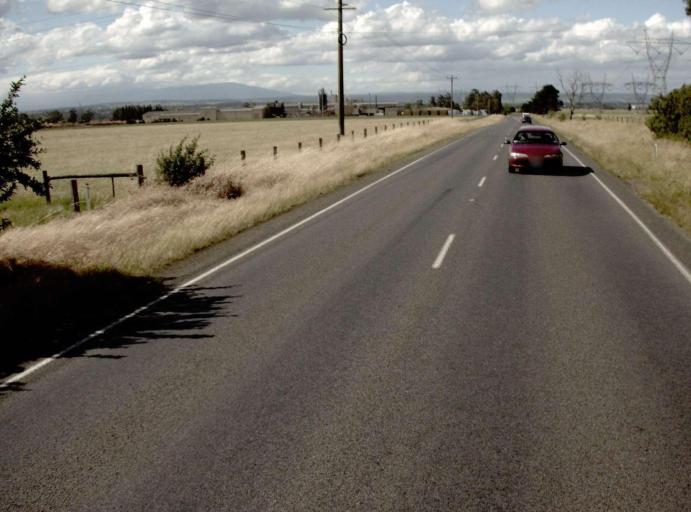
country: AU
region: Victoria
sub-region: Latrobe
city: Morwell
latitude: -38.2714
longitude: 146.4334
